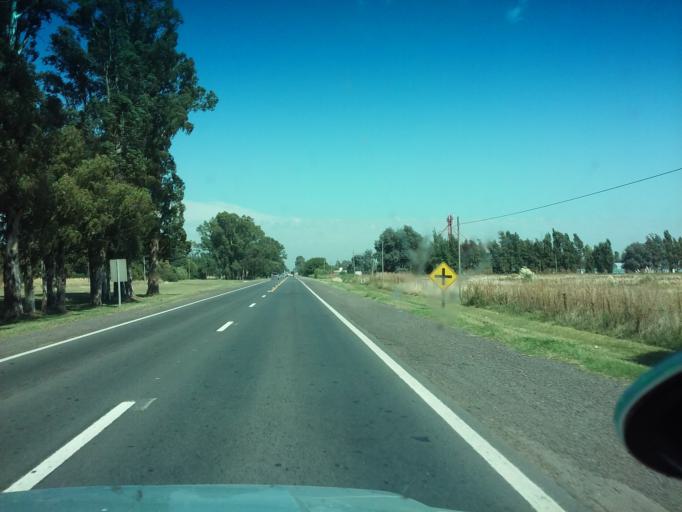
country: AR
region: Buenos Aires
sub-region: Partido de Nueve de Julio
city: Nueve de Julio
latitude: -35.4832
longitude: -60.8789
